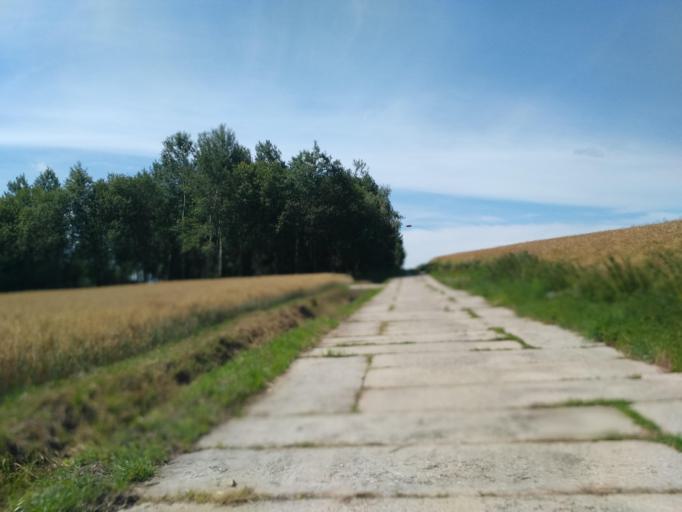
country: PL
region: Subcarpathian Voivodeship
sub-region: Powiat brzozowski
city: Haczow
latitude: 49.6564
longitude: 21.8713
